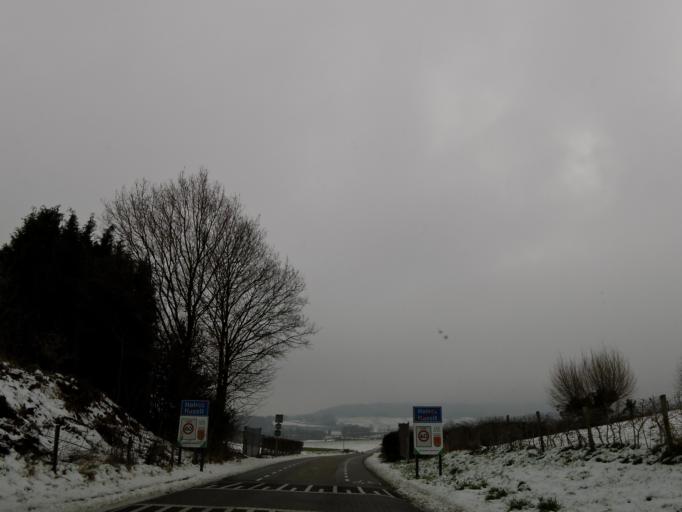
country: NL
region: Limburg
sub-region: Gemeente Vaals
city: Vaals
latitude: 50.7725
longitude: 5.9865
